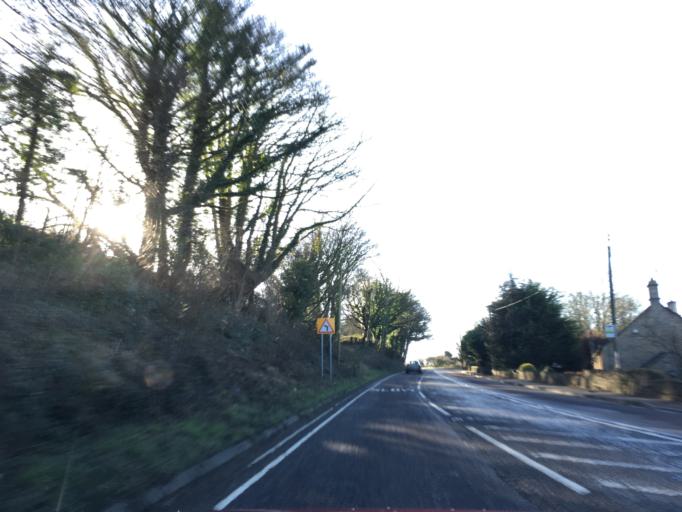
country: GB
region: England
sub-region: South Gloucestershire
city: Horton
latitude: 51.5287
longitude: -2.3525
